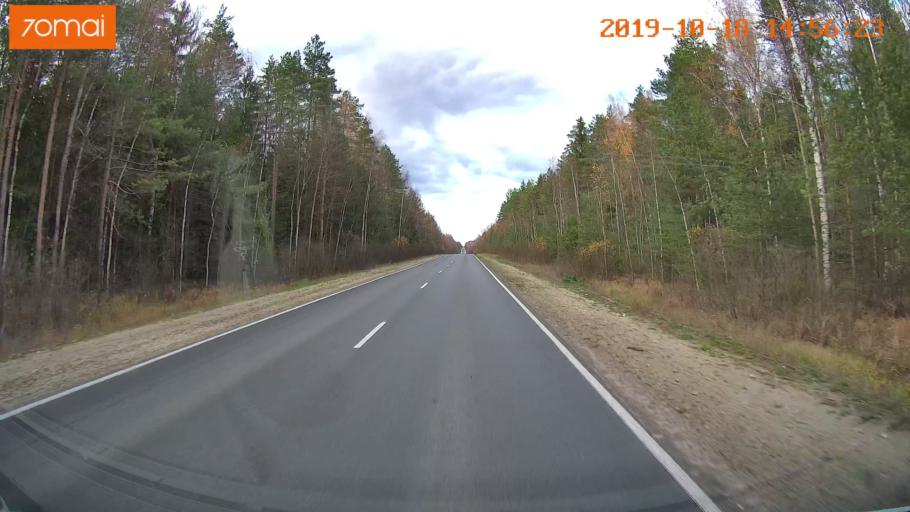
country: RU
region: Vladimir
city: Kurlovo
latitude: 55.4639
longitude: 40.5877
